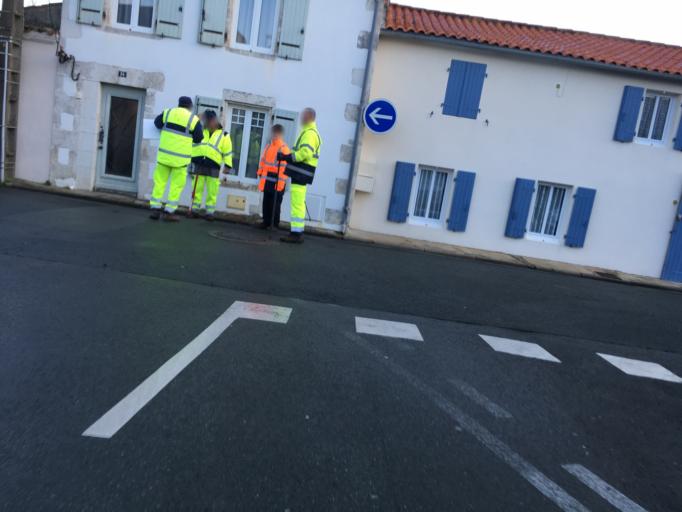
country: FR
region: Poitou-Charentes
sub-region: Departement de la Charente-Maritime
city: Nieul-sur-Mer
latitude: 46.2057
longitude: -1.1649
